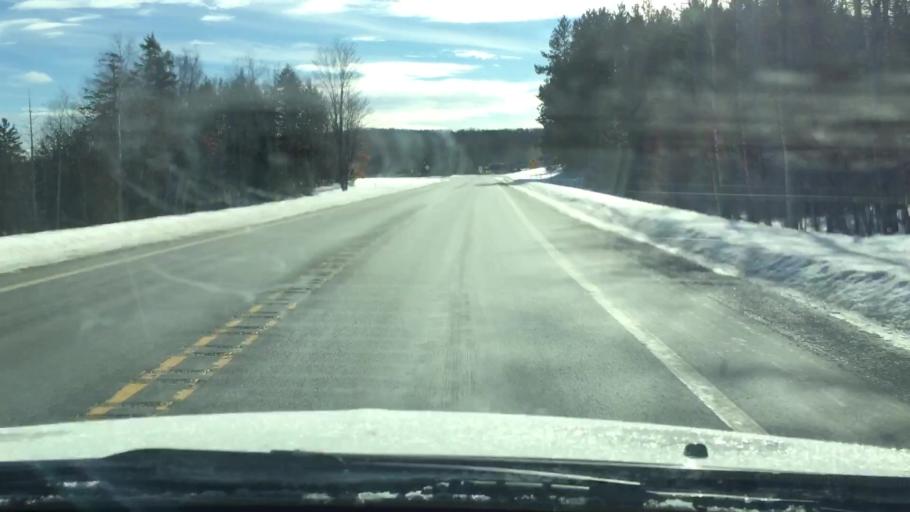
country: US
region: Michigan
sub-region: Antrim County
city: Mancelona
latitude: 44.9958
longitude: -85.0616
